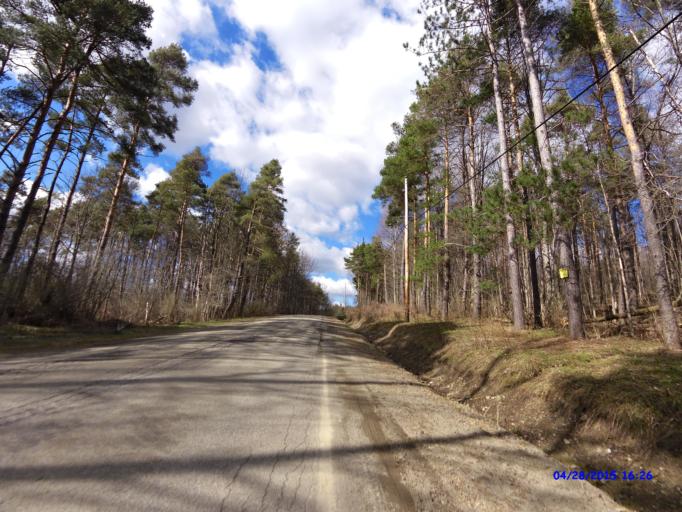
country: US
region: New York
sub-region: Cattaraugus County
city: Franklinville
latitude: 42.3824
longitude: -78.4416
